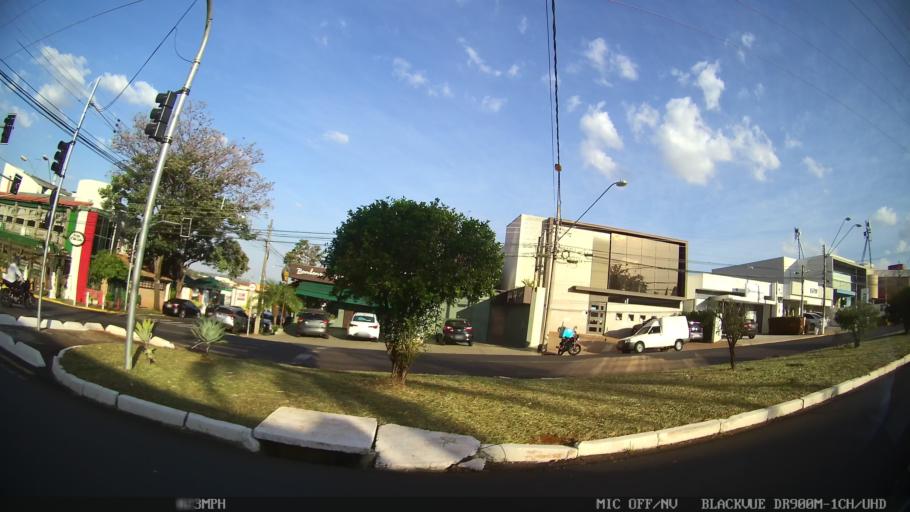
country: BR
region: Sao Paulo
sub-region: Ribeirao Preto
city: Ribeirao Preto
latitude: -21.1942
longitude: -47.8022
